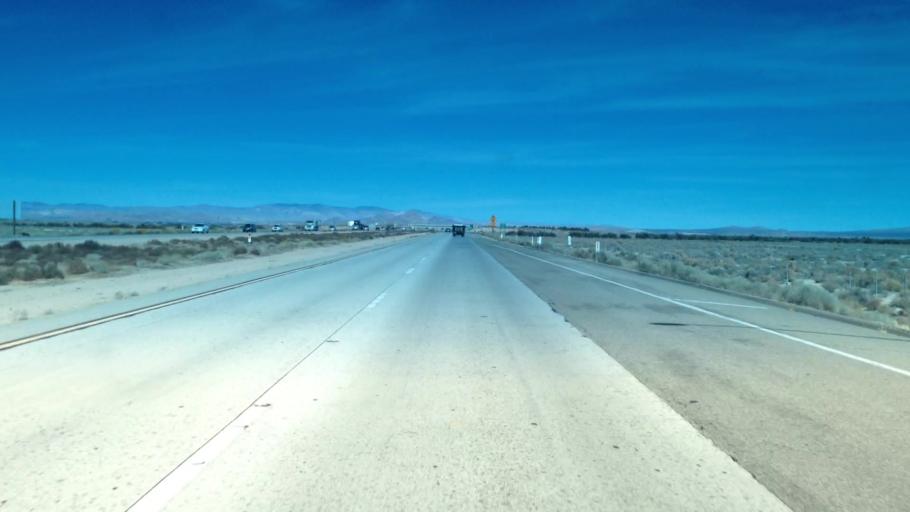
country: US
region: California
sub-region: Los Angeles County
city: Lancaster
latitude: 34.7366
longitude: -118.1701
